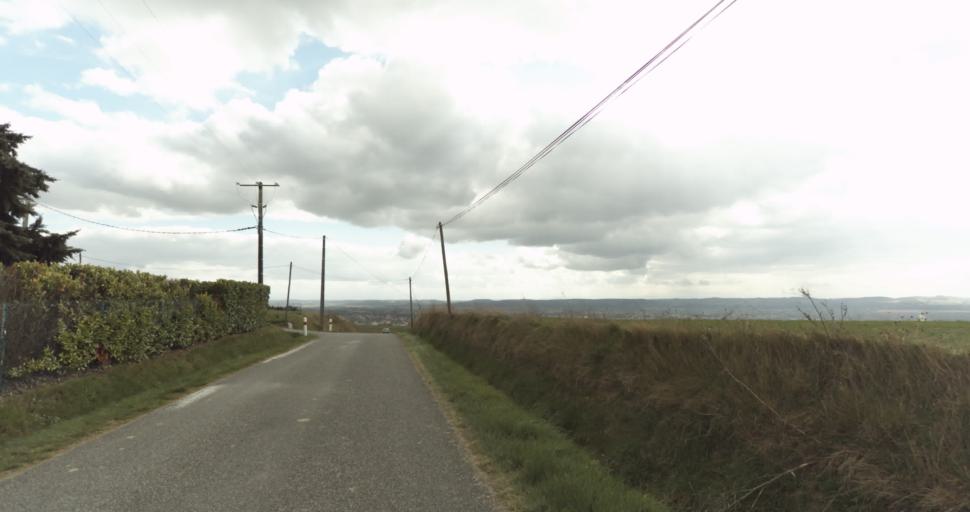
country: FR
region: Midi-Pyrenees
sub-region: Departement de la Haute-Garonne
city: Auterive
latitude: 43.3673
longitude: 1.4845
